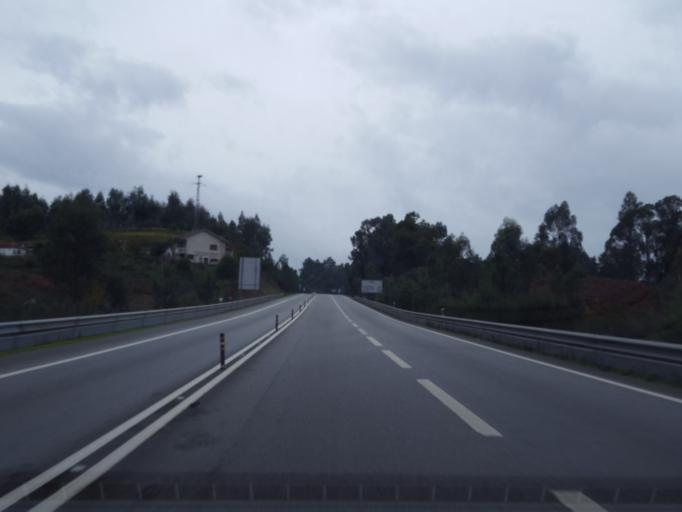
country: PT
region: Porto
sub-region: Marco de Canaveses
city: Marco de Canavezes
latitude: 41.2274
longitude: -8.1943
